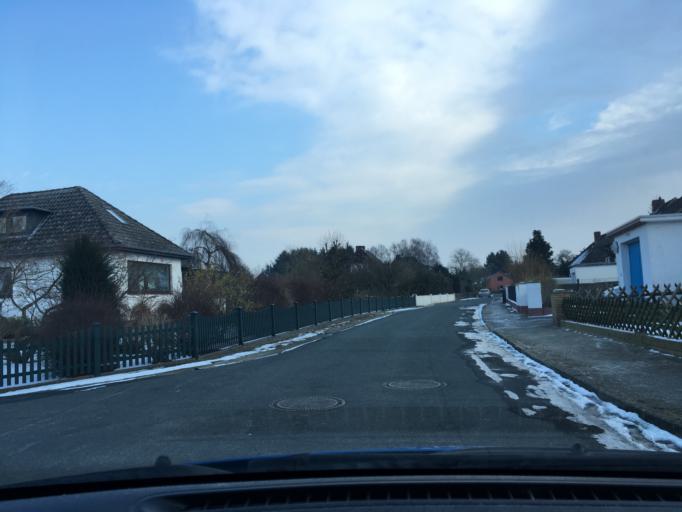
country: DE
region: Lower Saxony
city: Bienenbuttel
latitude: 53.1419
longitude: 10.4949
